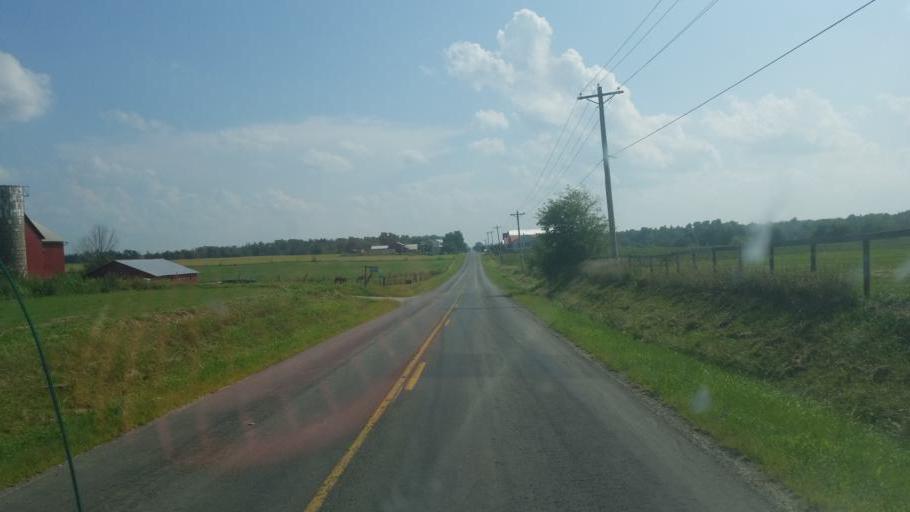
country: US
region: Ohio
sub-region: Wayne County
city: West Salem
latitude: 41.0540
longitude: -82.1629
